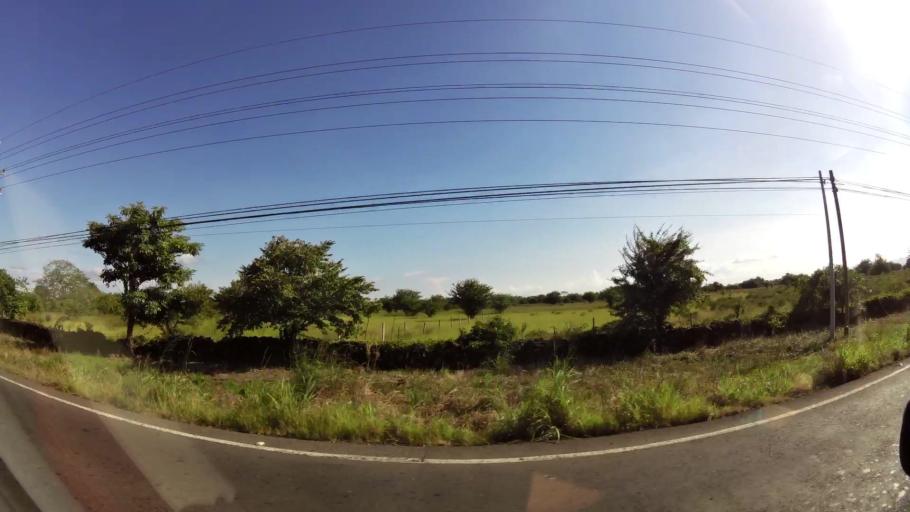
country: CR
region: Guanacaste
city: Sardinal
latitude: 10.5875
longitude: -85.5526
